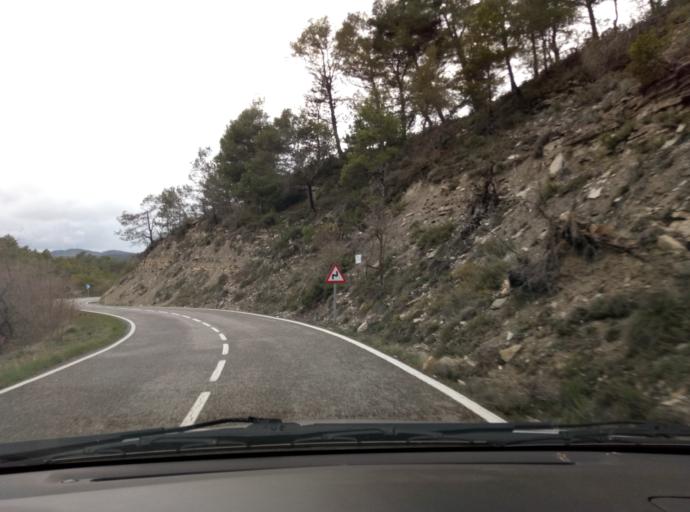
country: ES
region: Catalonia
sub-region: Provincia de Tarragona
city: Santa Coloma de Queralt
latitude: 41.5428
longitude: 1.3382
